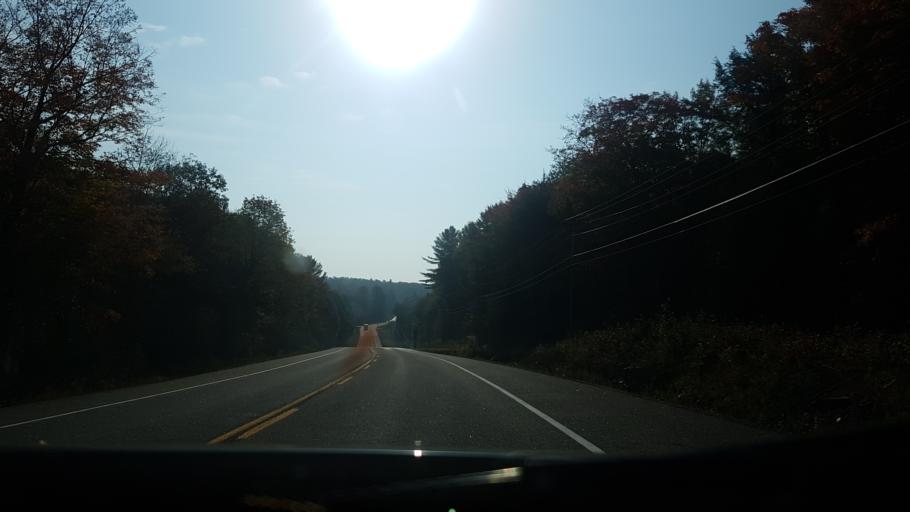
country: CA
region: Ontario
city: Bracebridge
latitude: 45.2420
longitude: -79.5904
